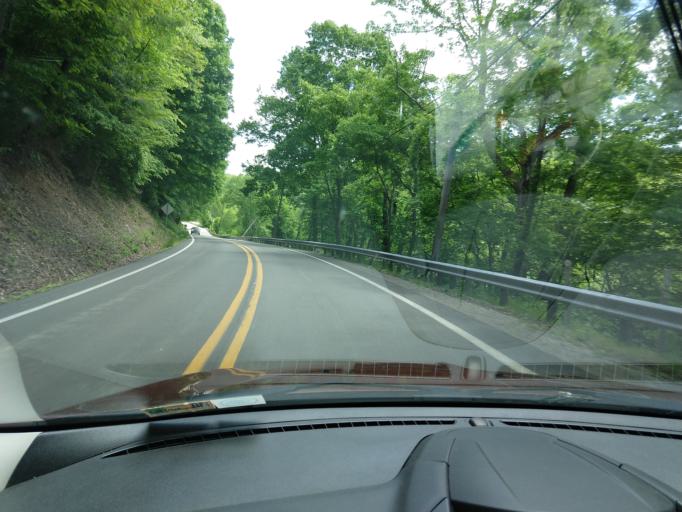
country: US
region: West Virginia
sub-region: Gilmer County
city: Glenville
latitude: 38.9167
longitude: -80.7552
